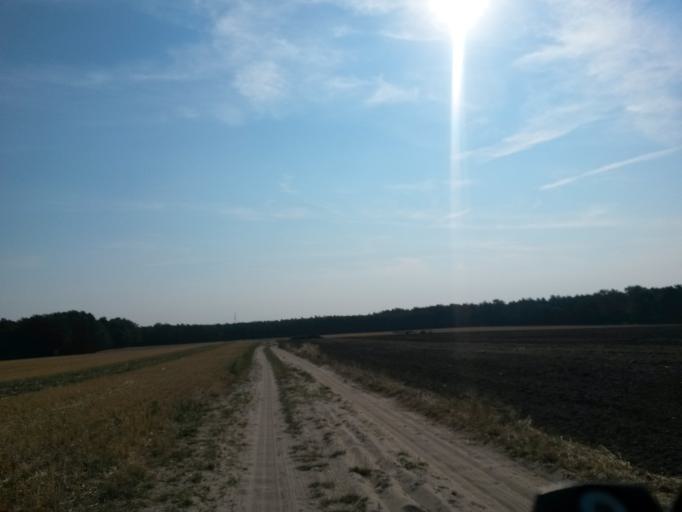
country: DE
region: Saxony-Anhalt
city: Nudersdorf
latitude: 51.9049
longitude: 12.5897
